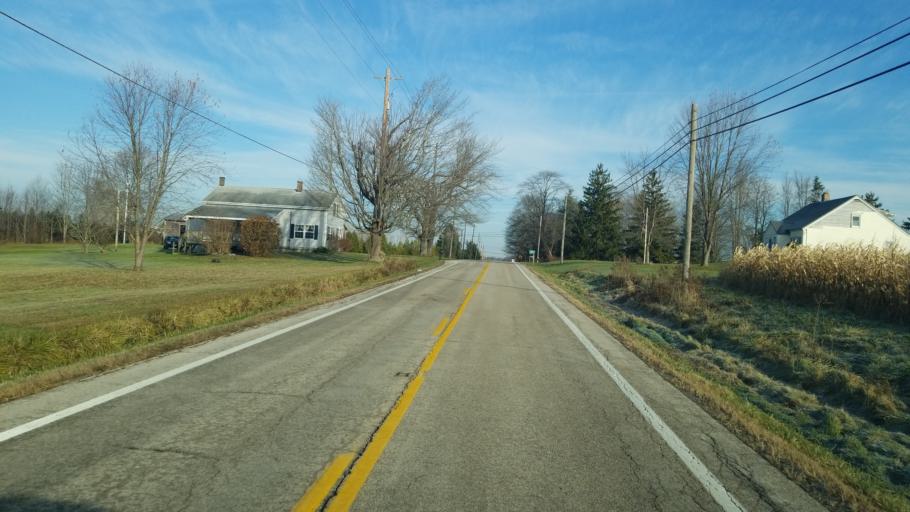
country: US
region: Ohio
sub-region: Ashtabula County
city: North Kingsville
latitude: 41.8193
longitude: -80.6640
